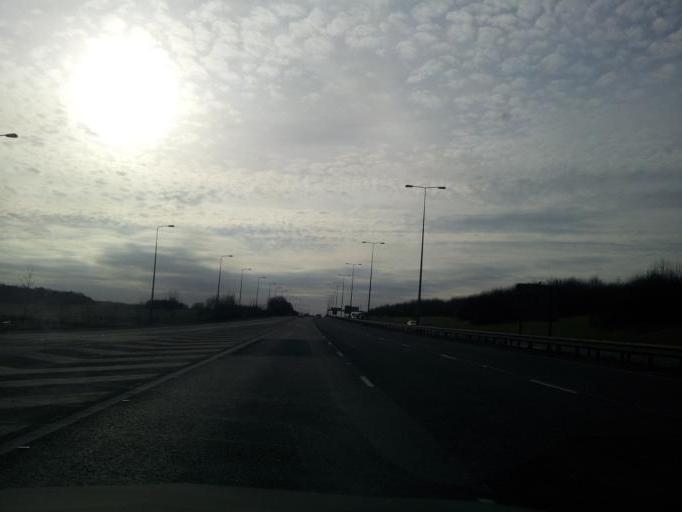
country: GB
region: England
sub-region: Peterborough
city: Castor
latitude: 52.5317
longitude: -0.3163
